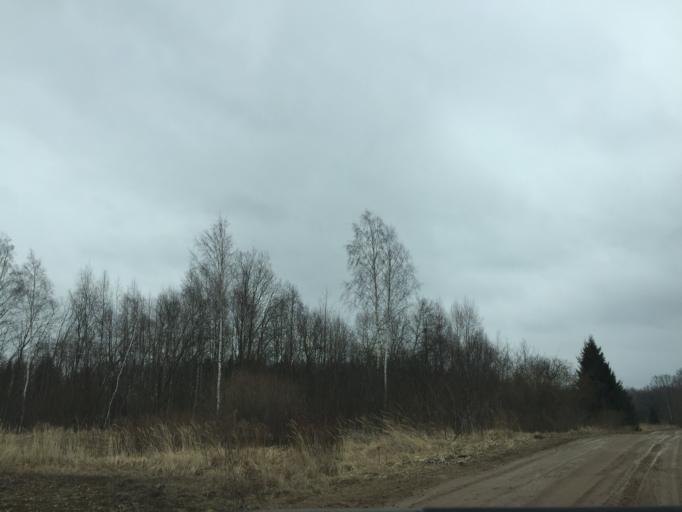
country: LV
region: Lielvarde
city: Lielvarde
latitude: 56.7574
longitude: 24.8167
